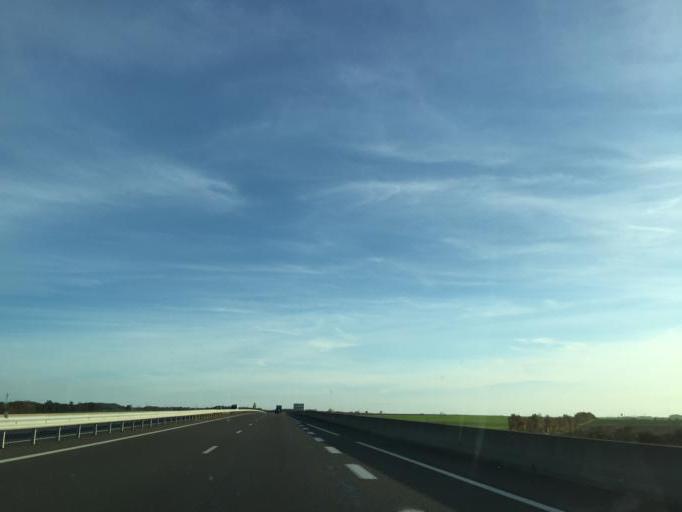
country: FR
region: Rhone-Alpes
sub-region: Departement du Rhone
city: Pusignan
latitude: 45.7618
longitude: 5.0879
